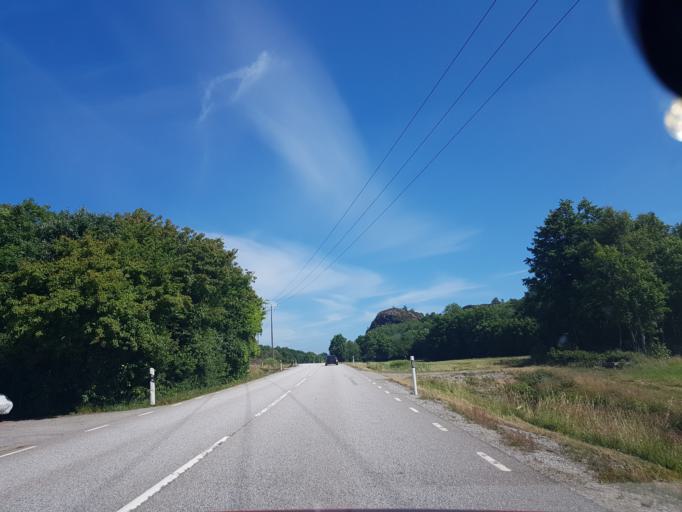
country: SE
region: Vaestra Goetaland
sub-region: Lysekils Kommun
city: Lysekil
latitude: 58.1578
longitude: 11.4723
